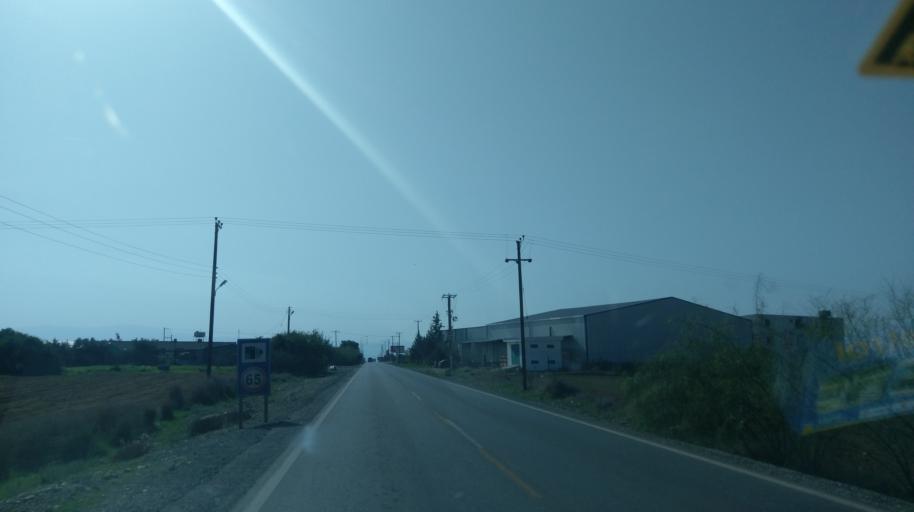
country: CY
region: Lefkosia
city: Morfou
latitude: 35.2363
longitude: 33.0216
